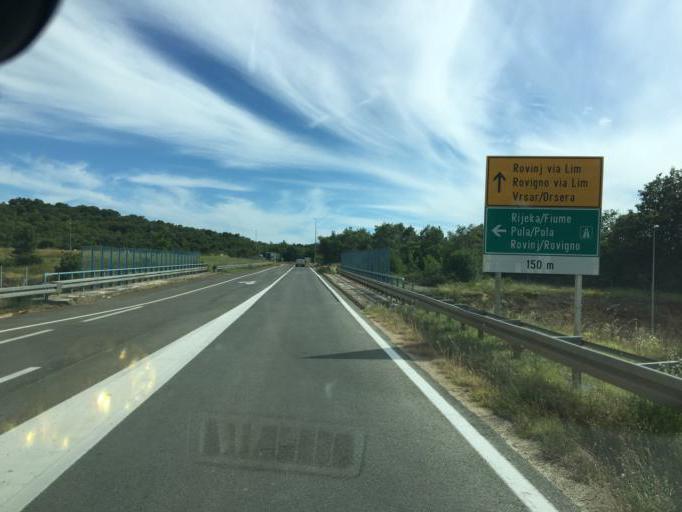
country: HR
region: Istarska
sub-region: Grad Rovinj
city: Rovinj
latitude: 45.1517
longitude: 13.7399
